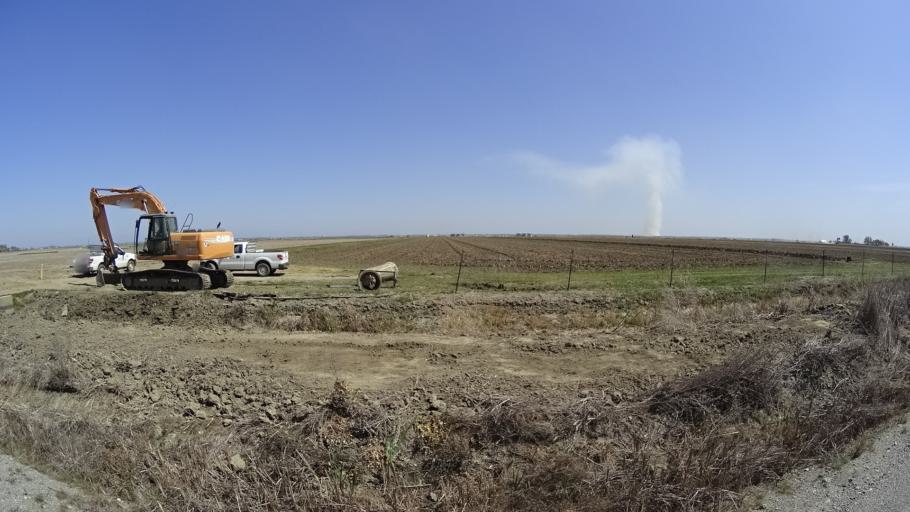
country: US
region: California
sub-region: Glenn County
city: Willows
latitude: 39.5307
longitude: -122.0887
